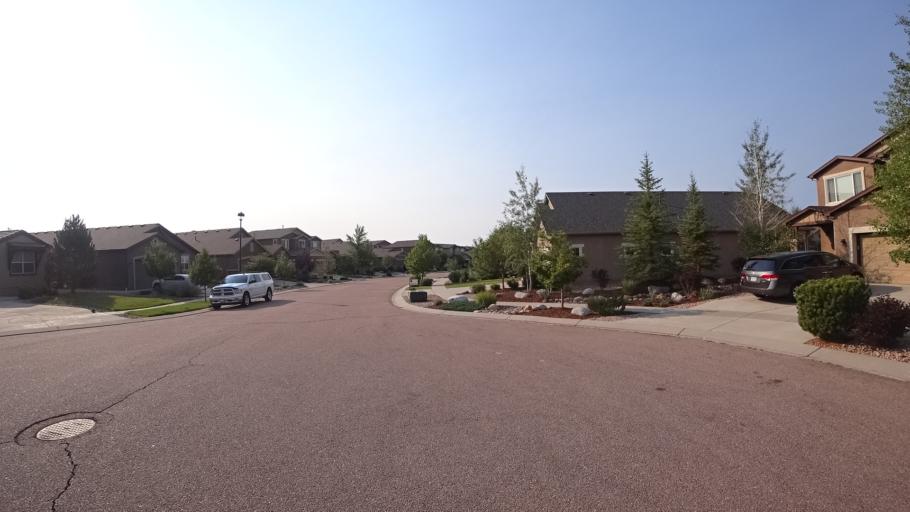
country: US
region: Colorado
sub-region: El Paso County
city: Black Forest
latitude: 38.9760
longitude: -104.7392
